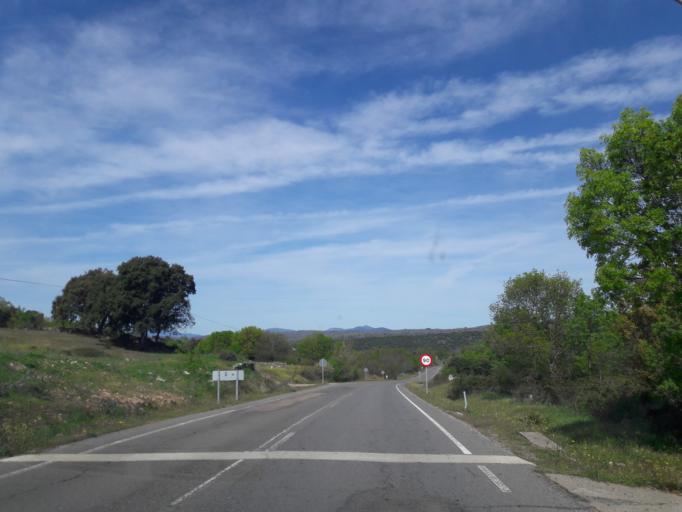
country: ES
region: Castille and Leon
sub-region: Provincia de Salamanca
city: Ledrada
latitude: 40.4718
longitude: -5.7220
